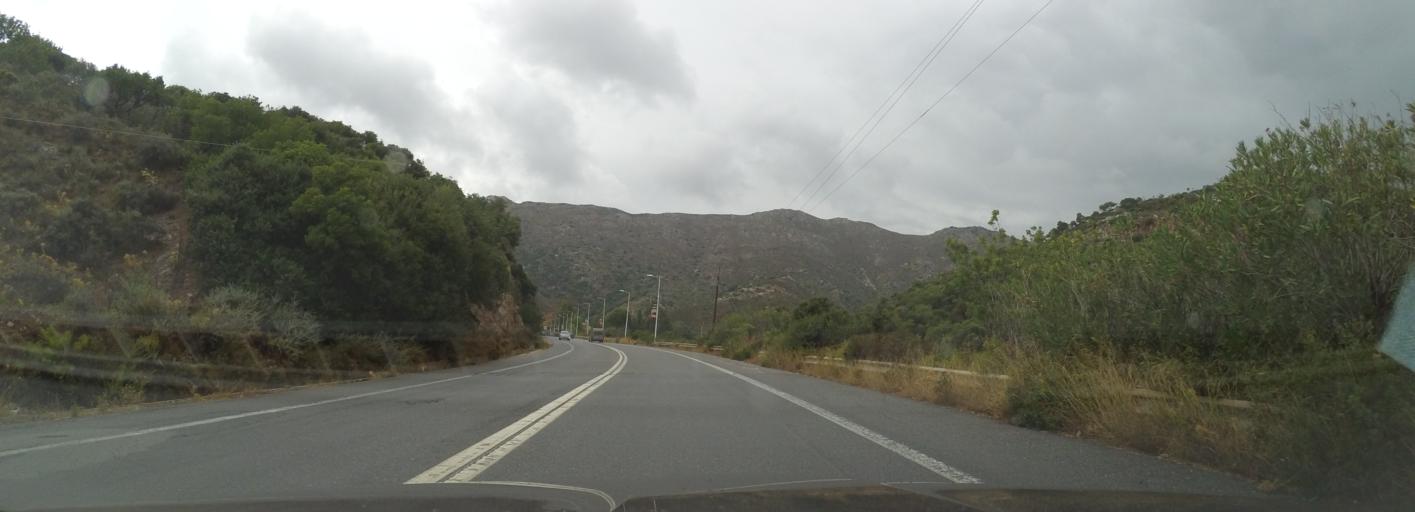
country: GR
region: Crete
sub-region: Nomos Rethymnis
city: Anogeia
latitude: 35.3866
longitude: 24.9193
